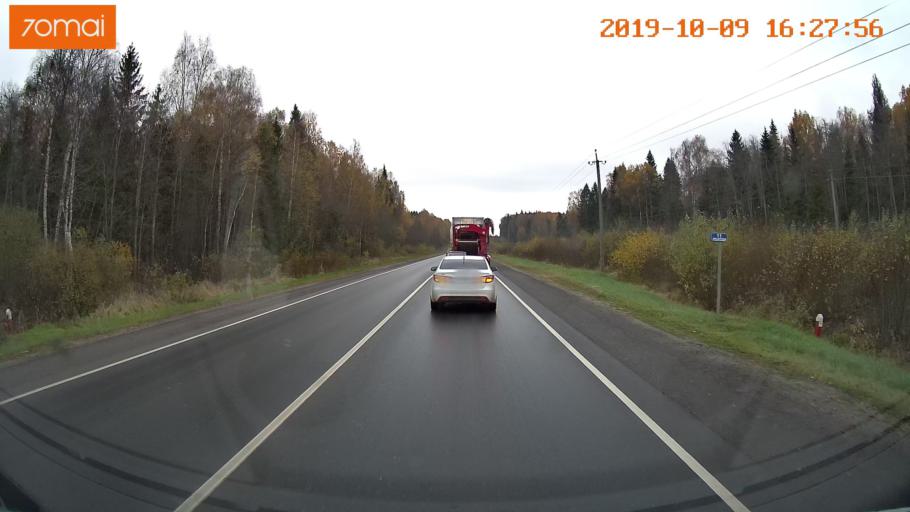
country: RU
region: Kostroma
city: Oktyabr'skiy
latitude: 57.6311
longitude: 40.9300
